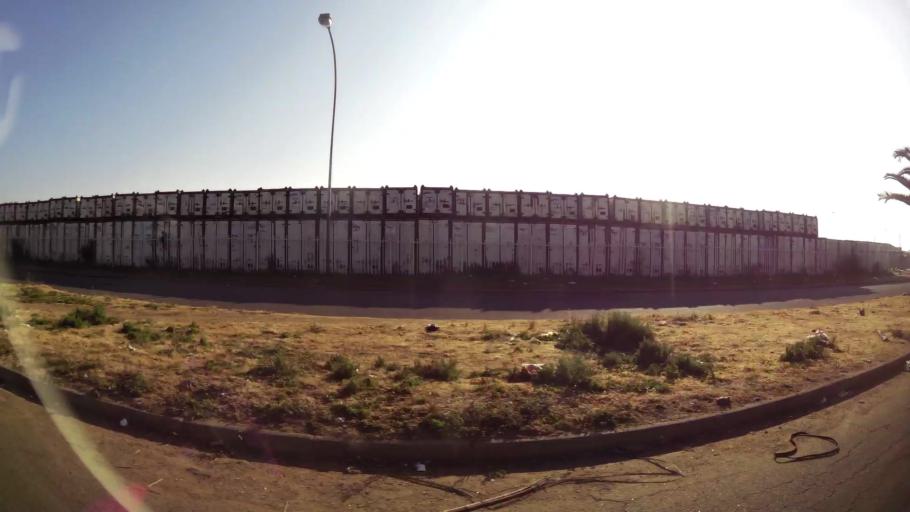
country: ZA
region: Orange Free State
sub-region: Mangaung Metropolitan Municipality
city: Bloemfontein
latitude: -29.1328
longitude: 26.2607
